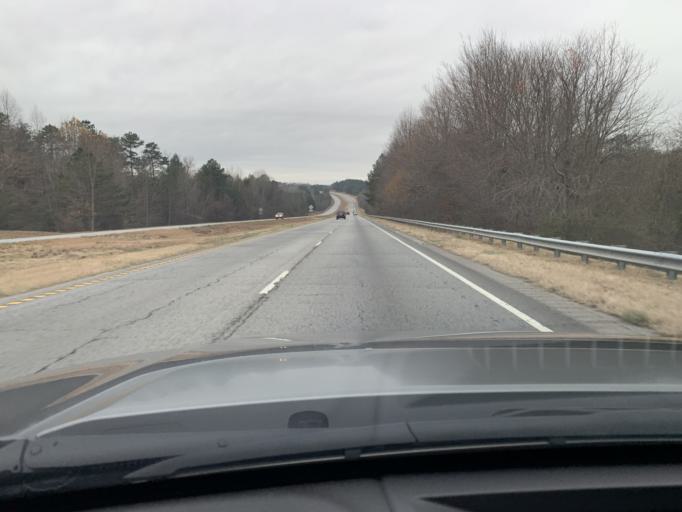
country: US
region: Georgia
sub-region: Habersham County
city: Demorest
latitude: 34.5647
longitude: -83.5069
